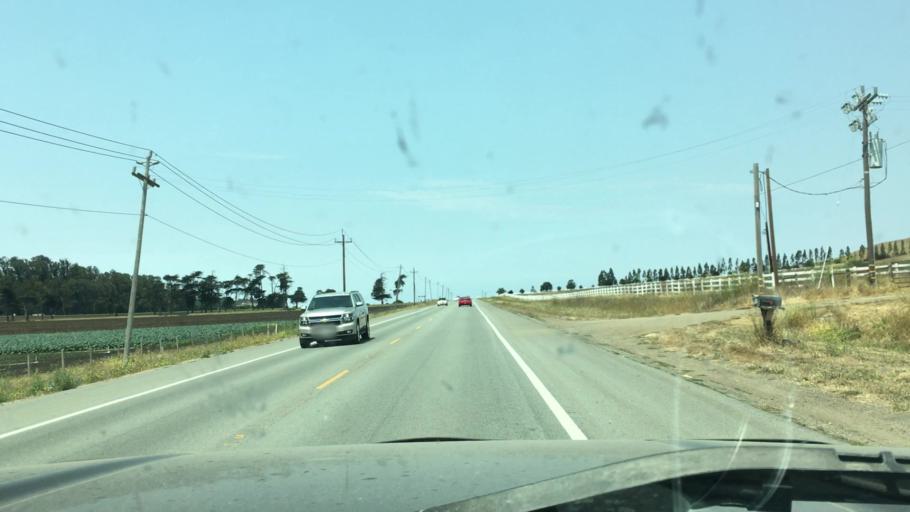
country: US
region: California
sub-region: San Luis Obispo County
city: San Luis Obispo
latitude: 35.2846
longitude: -120.7327
